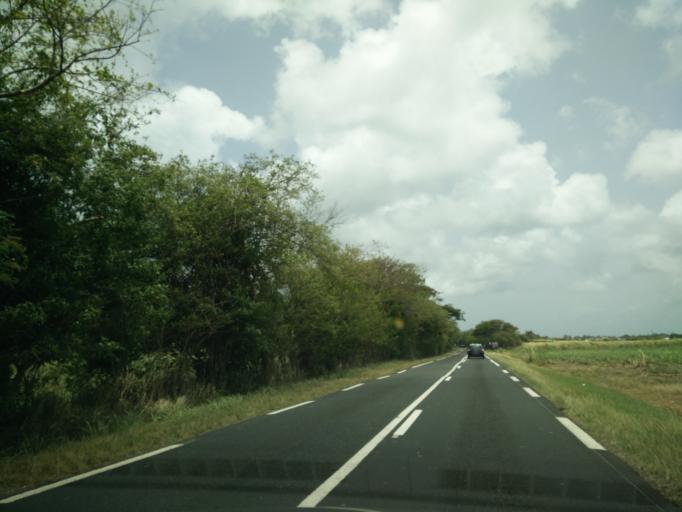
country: GP
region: Guadeloupe
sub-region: Guadeloupe
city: Port-Louis
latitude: 16.4071
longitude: -61.5087
